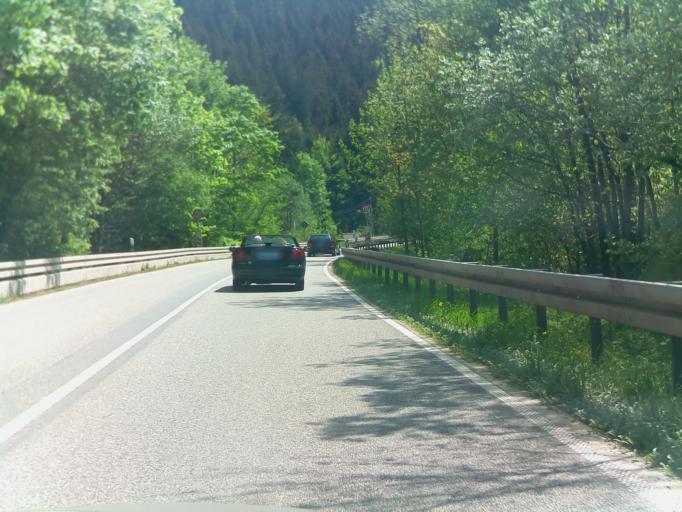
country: DE
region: Thuringia
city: Ilfeld
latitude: 51.6260
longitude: 10.8182
